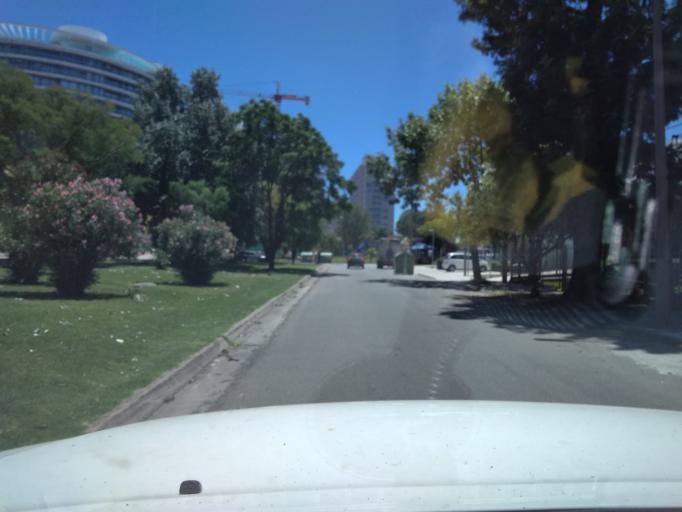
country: UY
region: Canelones
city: Paso de Carrasco
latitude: -34.8889
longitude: -56.1062
